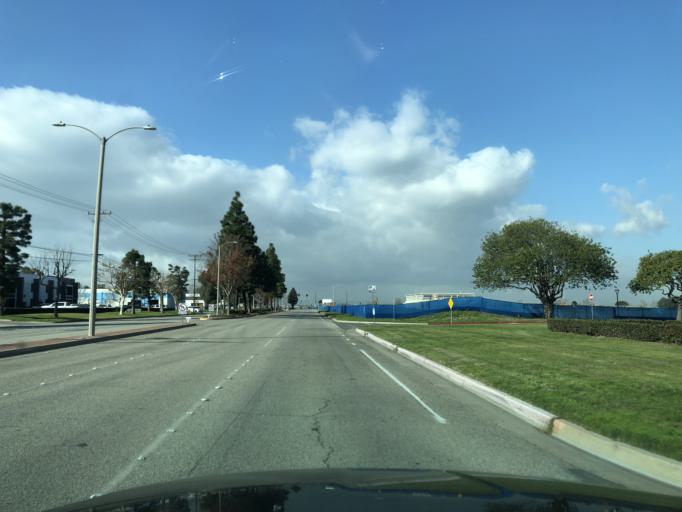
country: US
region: California
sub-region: Orange County
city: Westminster
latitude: 33.7445
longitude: -118.0359
